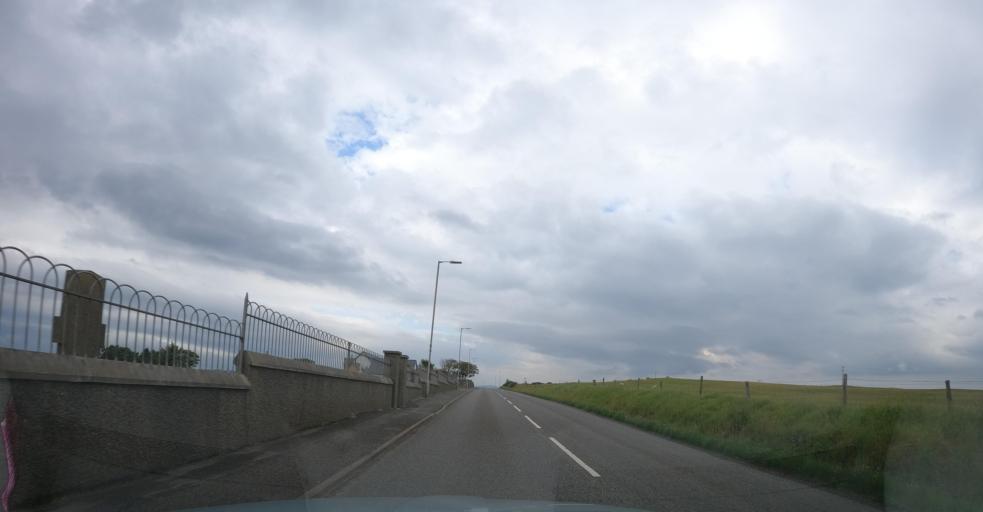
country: GB
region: Scotland
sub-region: Eilean Siar
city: Stornoway
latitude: 58.2072
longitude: -6.3587
